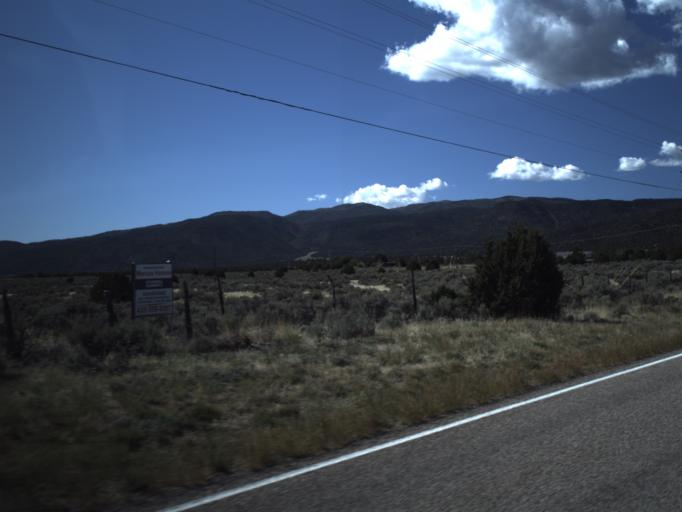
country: US
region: Utah
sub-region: Iron County
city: Cedar City
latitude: 37.6464
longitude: -113.2420
